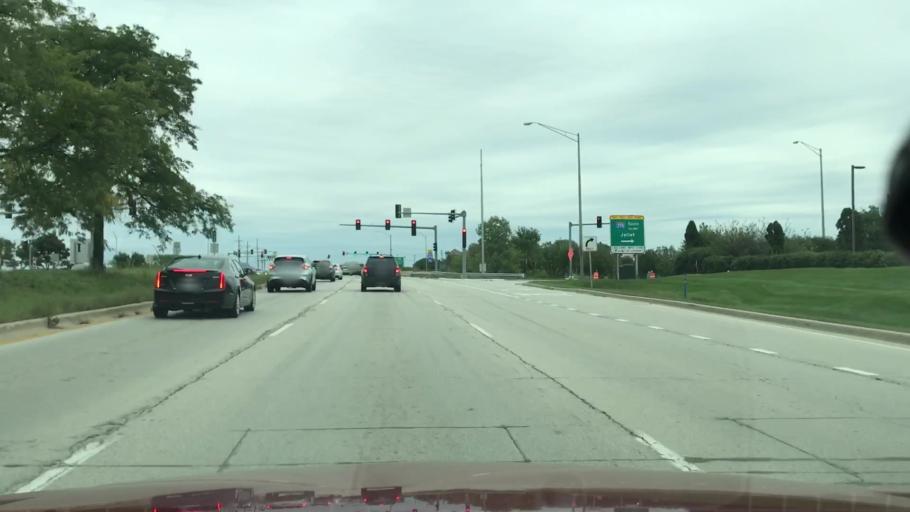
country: US
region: Illinois
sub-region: DuPage County
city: Downers Grove
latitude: 41.8328
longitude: -88.0309
